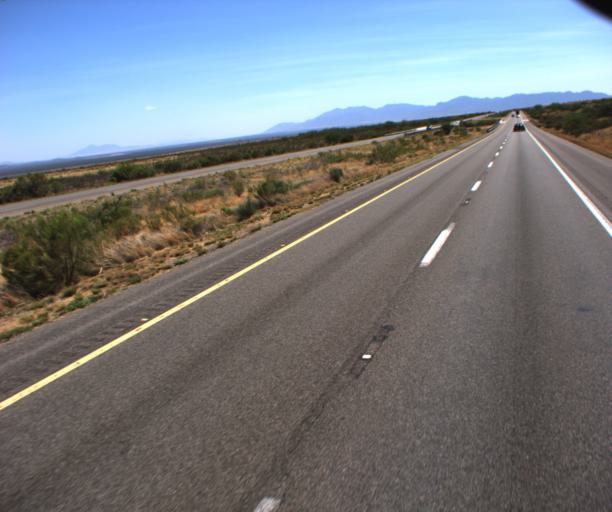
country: US
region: Arizona
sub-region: Cochise County
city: Whetstone
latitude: 31.8193
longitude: -110.3471
